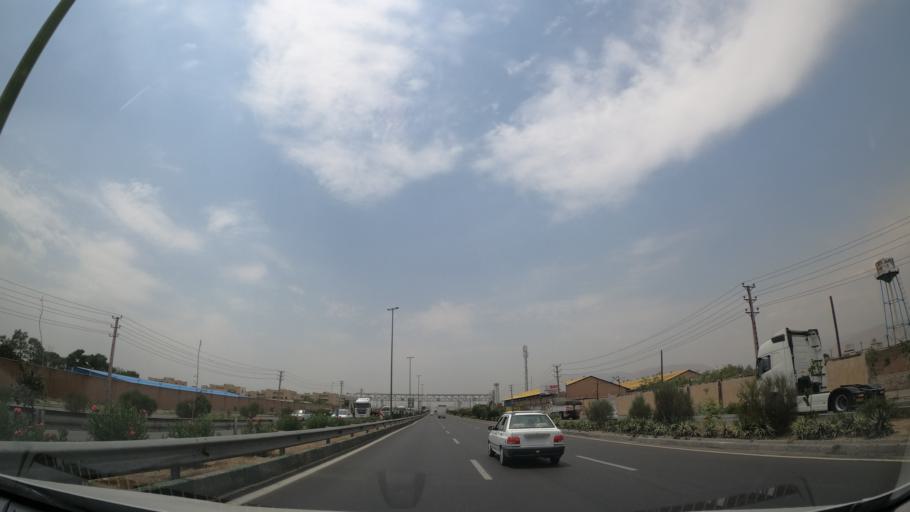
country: IR
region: Tehran
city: Shahr-e Qods
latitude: 35.6951
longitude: 51.2045
